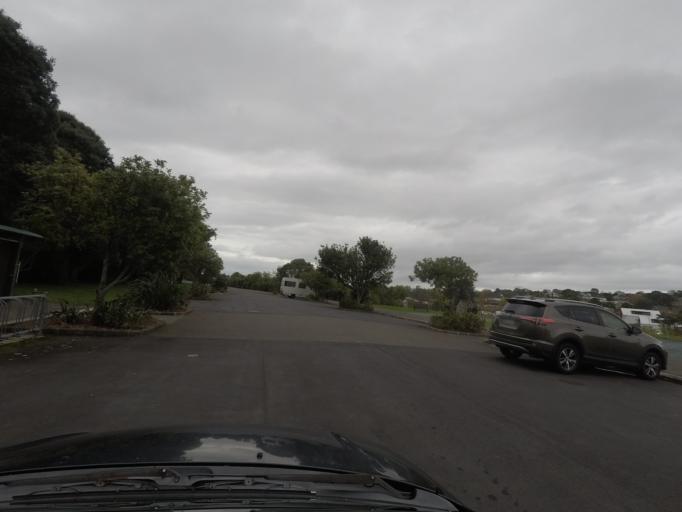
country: NZ
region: Auckland
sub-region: Auckland
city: Auckland
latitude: -36.8642
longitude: 174.7840
